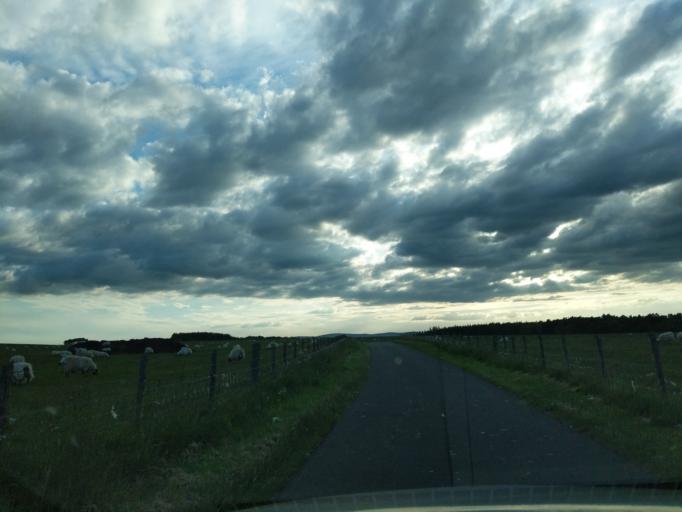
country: GB
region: Scotland
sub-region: Midlothian
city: Bonnyrigg
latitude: 55.7644
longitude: -3.1327
